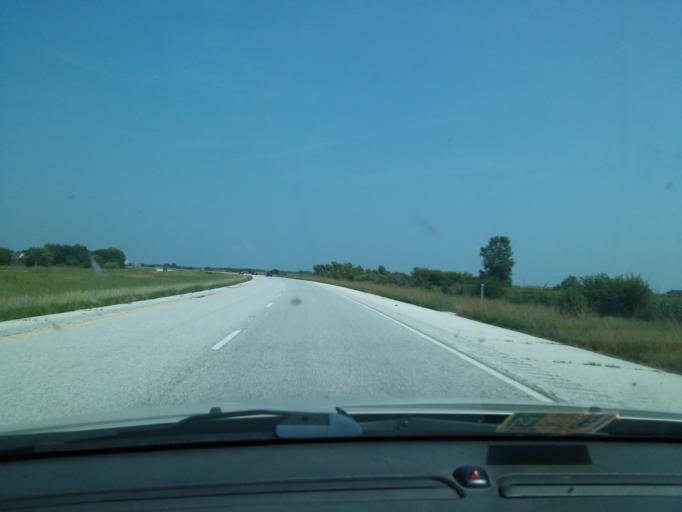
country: US
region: Illinois
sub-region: Morgan County
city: South Jacksonville
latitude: 39.6865
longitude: -90.2100
